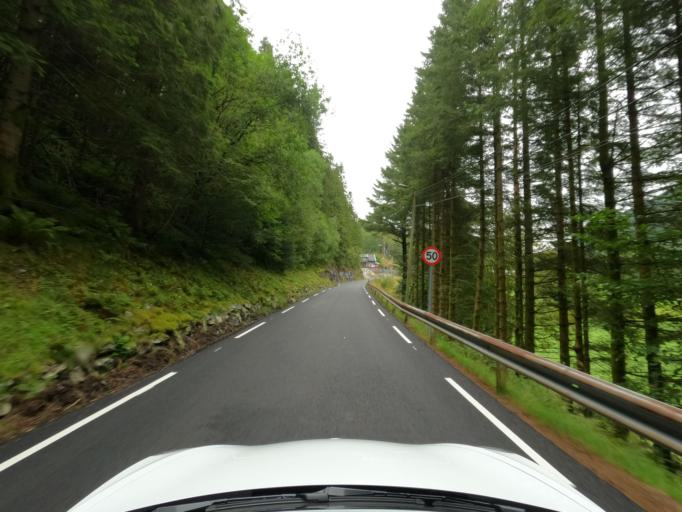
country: NO
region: Hordaland
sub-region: Bergen
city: Espeland
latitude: 60.3632
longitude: 5.4873
